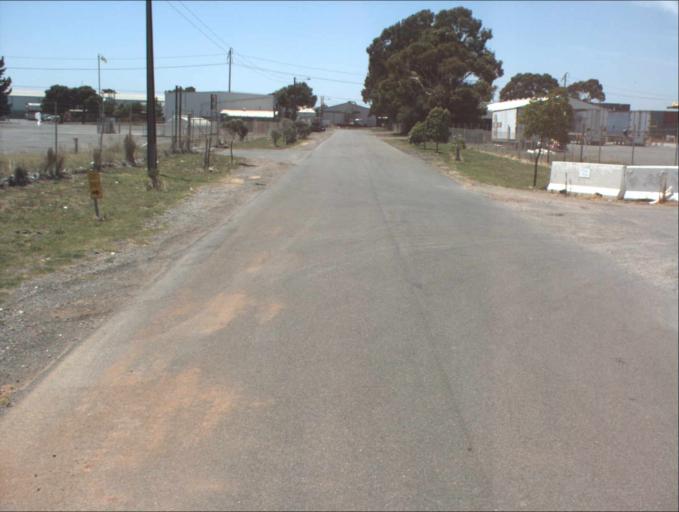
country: AU
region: South Australia
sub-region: Port Adelaide Enfield
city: Alberton
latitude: -34.8394
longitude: 138.5302
